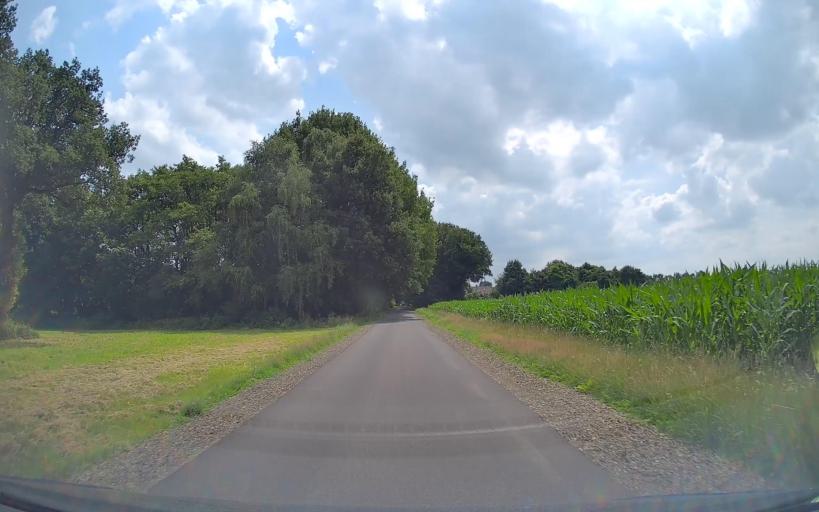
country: DE
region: Lower Saxony
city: Friesoythe
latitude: 52.9858
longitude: 7.8842
